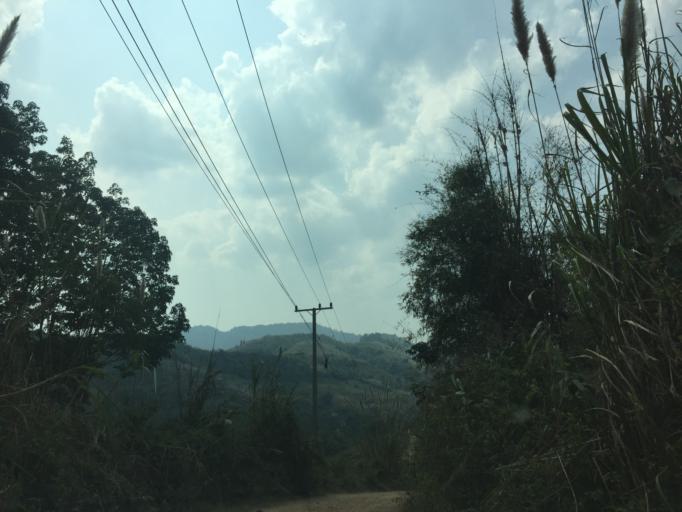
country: TH
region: Nan
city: Thung Chang
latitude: 19.7319
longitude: 100.7321
